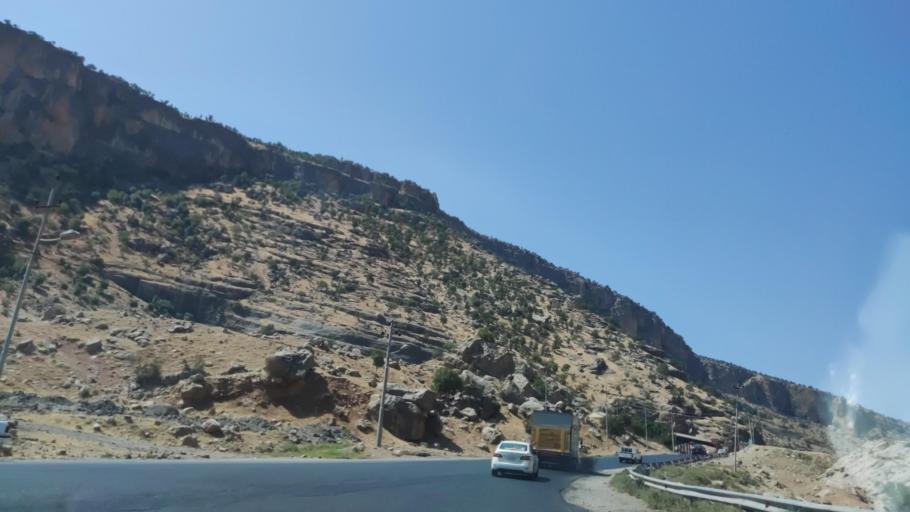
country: IQ
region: Arbil
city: Ruwandiz
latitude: 36.6301
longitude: 44.4419
